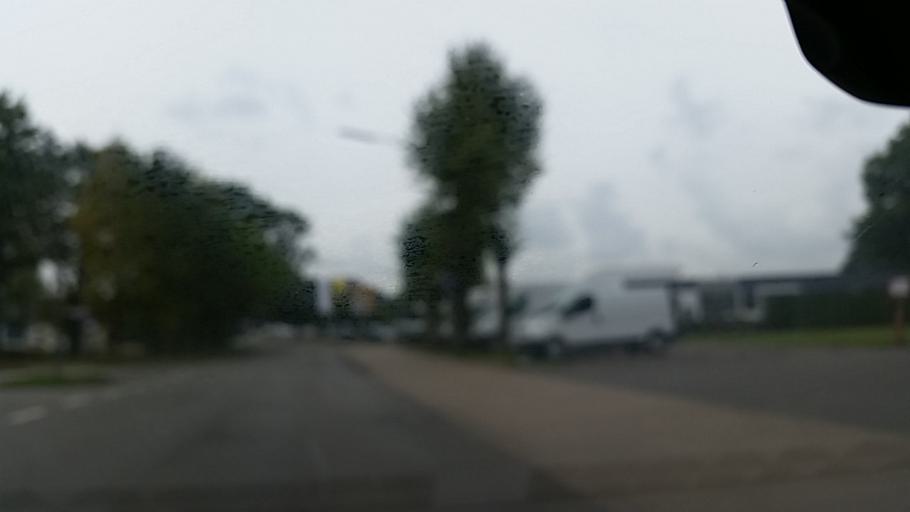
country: DE
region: Hamburg
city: Hummelsbuettel
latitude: 53.6865
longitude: 10.0458
